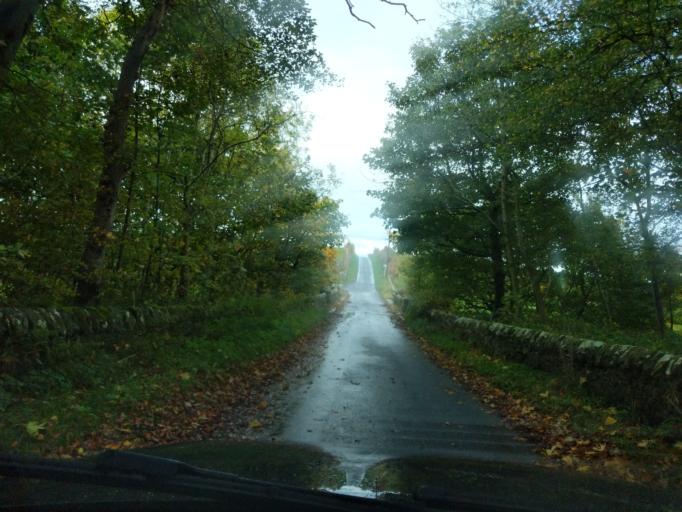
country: GB
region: Scotland
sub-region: Fife
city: Pittenweem
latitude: 56.2874
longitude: -2.7427
